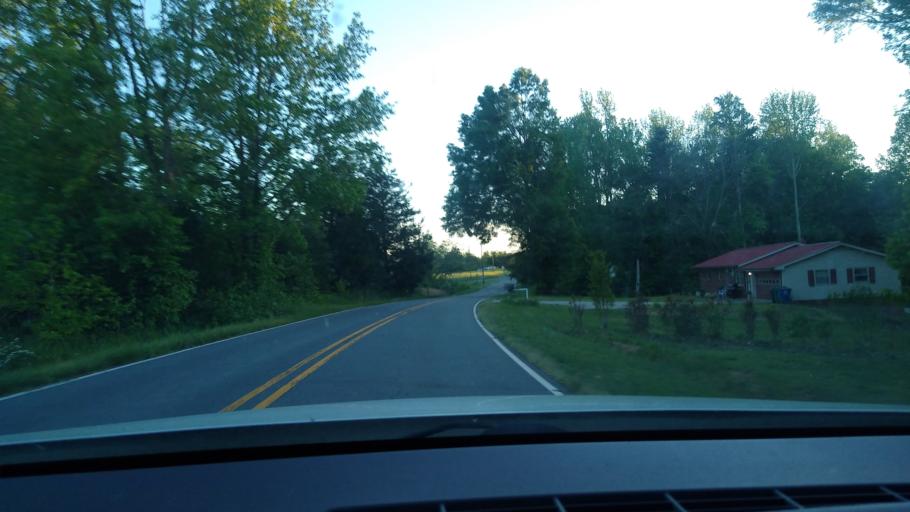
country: US
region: North Carolina
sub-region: Rockingham County
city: Reidsville
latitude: 36.3393
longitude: -79.5764
